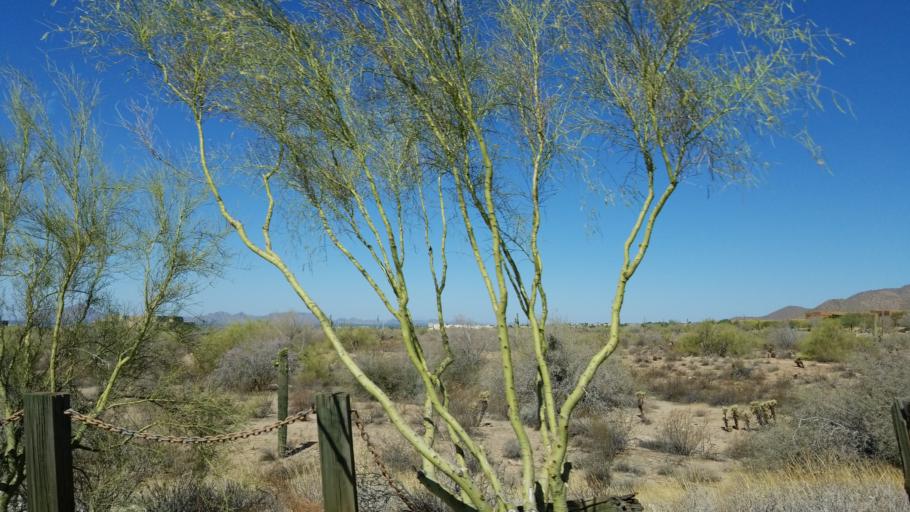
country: US
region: Arizona
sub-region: Maricopa County
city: Fountain Hills
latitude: 33.5886
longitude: -111.7875
